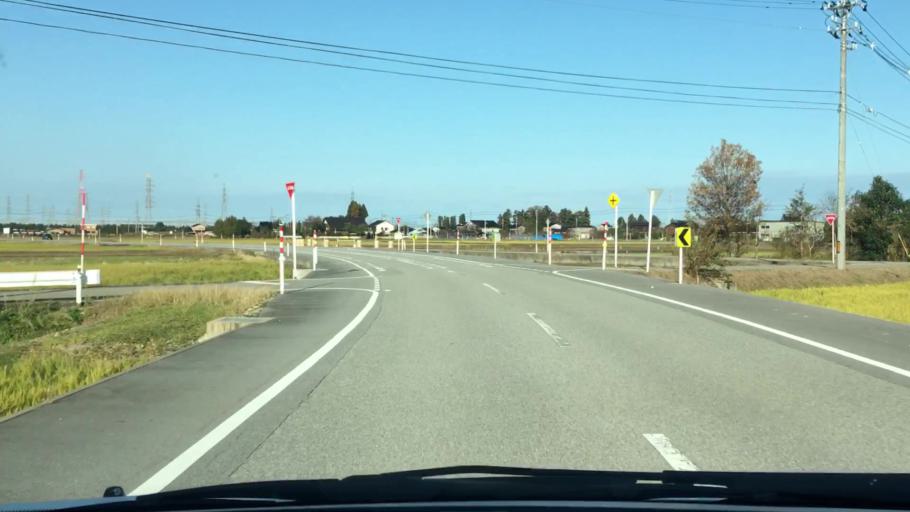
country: JP
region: Toyama
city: Kamiichi
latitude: 36.7082
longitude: 137.3235
